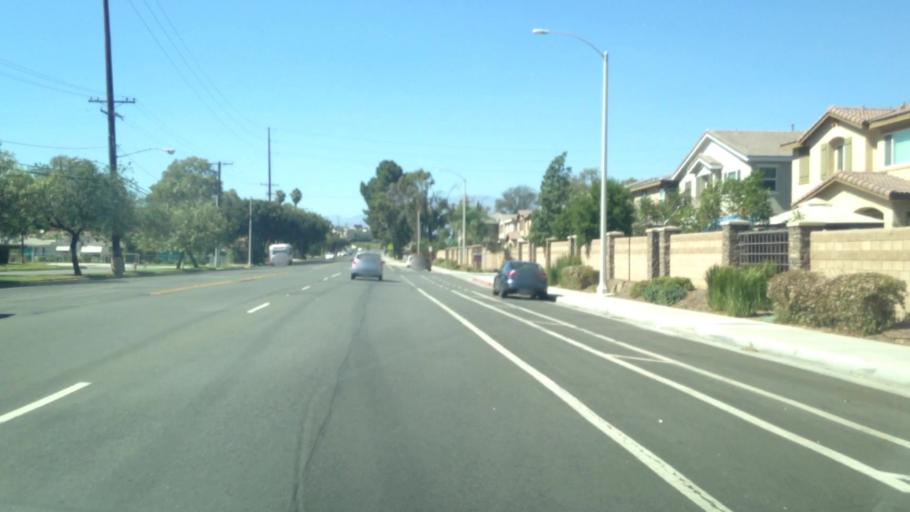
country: US
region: California
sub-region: Riverside County
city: Riverside
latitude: 33.9412
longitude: -117.4309
